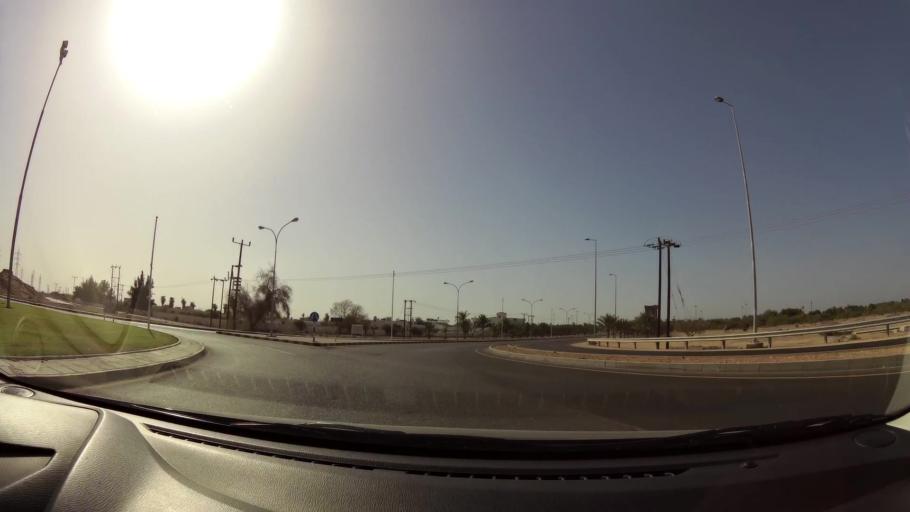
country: OM
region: Muhafazat Masqat
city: As Sib al Jadidah
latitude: 23.5818
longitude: 58.2529
